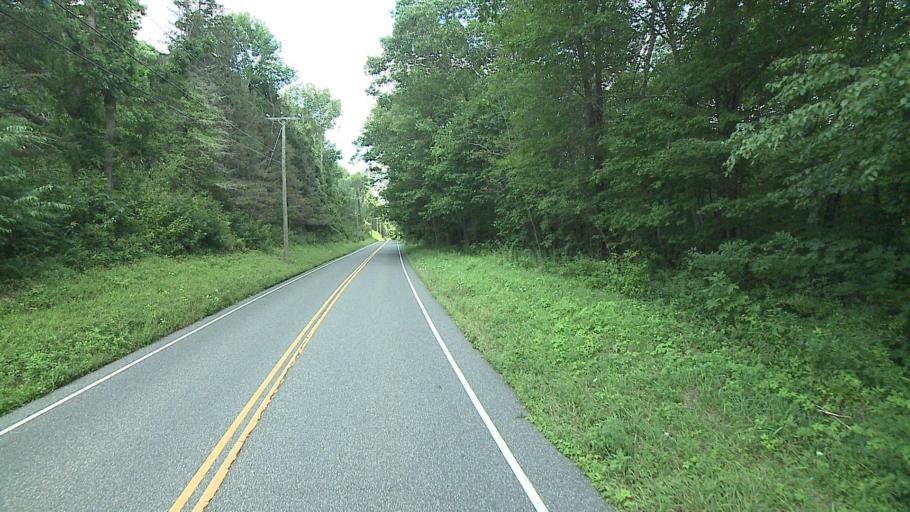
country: US
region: Connecticut
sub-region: Litchfield County
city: Bethlehem Village
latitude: 41.6653
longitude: -73.2676
